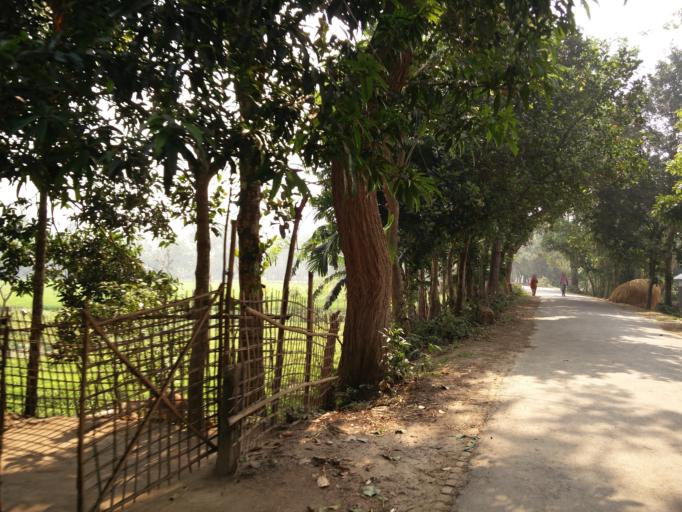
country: BD
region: Dhaka
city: Muktagacha
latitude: 24.9100
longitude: 90.1602
